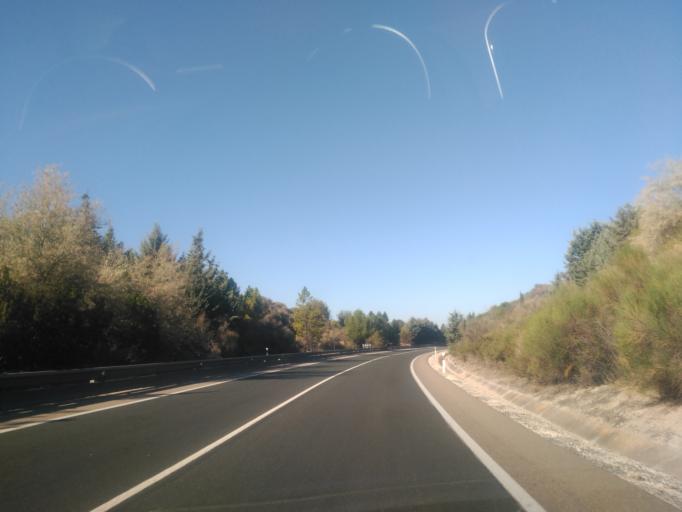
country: ES
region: Castille and Leon
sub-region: Provincia de Valladolid
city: Quintanilla de Onesimo
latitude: 41.6186
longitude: -4.3609
